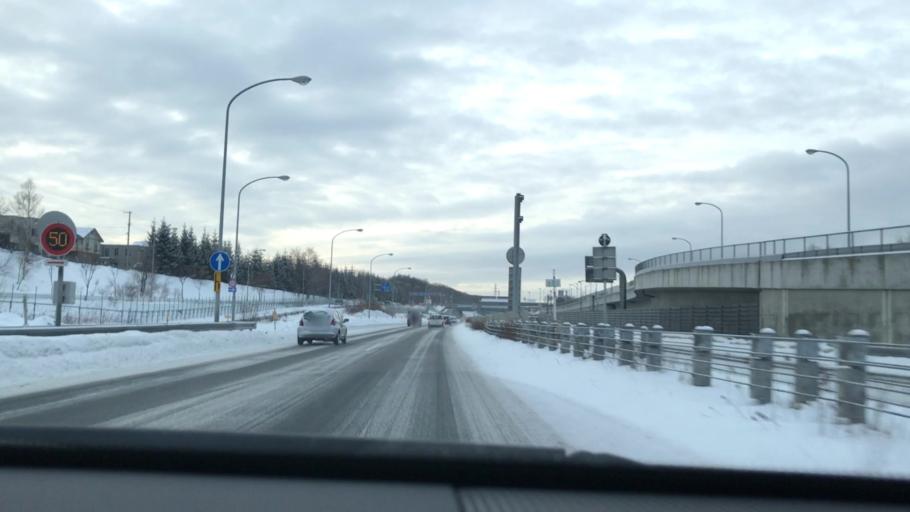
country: JP
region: Hokkaido
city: Kitahiroshima
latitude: 43.0136
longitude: 141.4649
